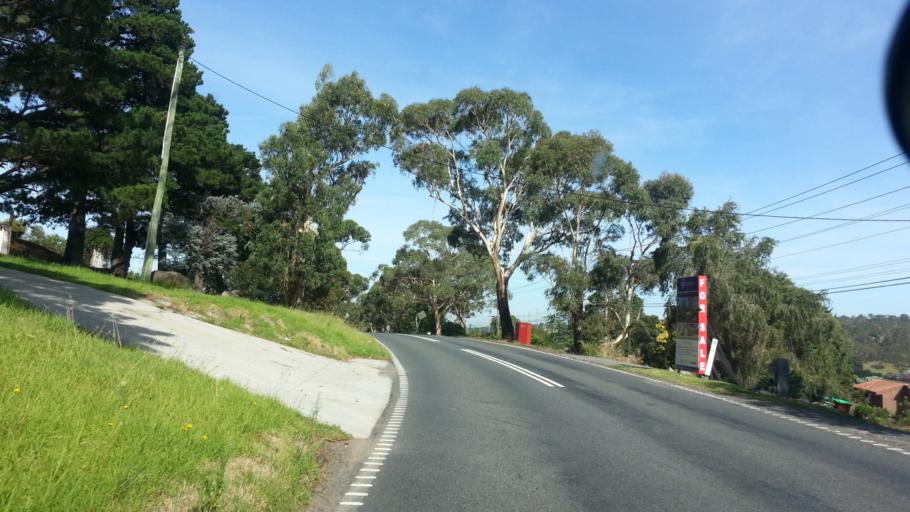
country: AU
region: Victoria
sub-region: Casey
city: Endeavour Hills
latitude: -37.9600
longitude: 145.2777
